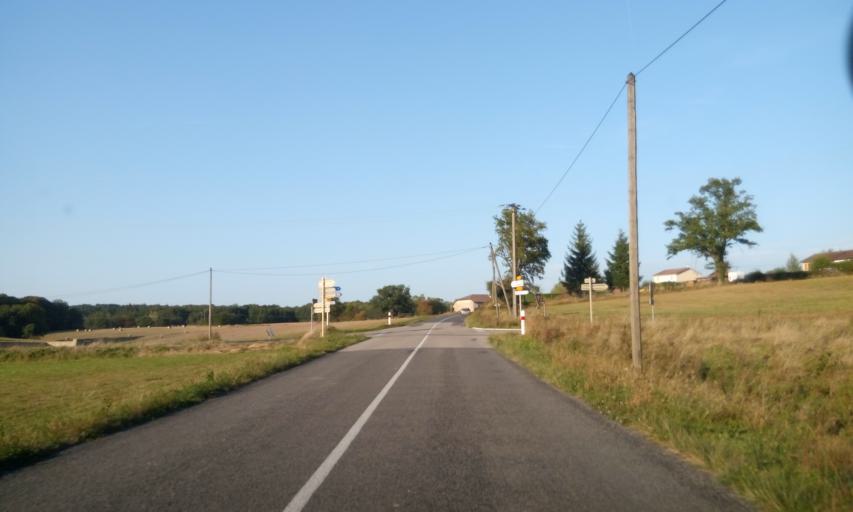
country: FR
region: Rhone-Alpes
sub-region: Departement de l'Ain
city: Priay
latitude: 46.0273
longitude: 5.2914
